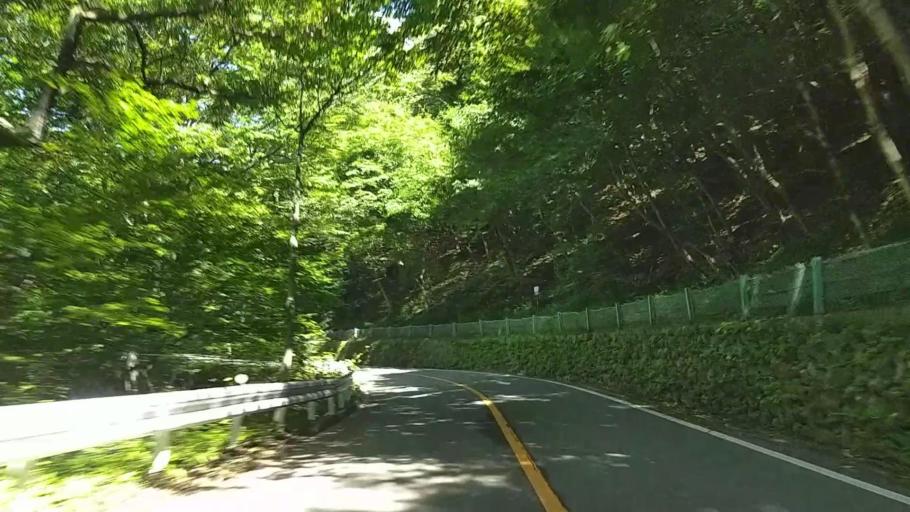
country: JP
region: Gunma
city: Annaka
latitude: 36.3525
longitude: 138.6750
